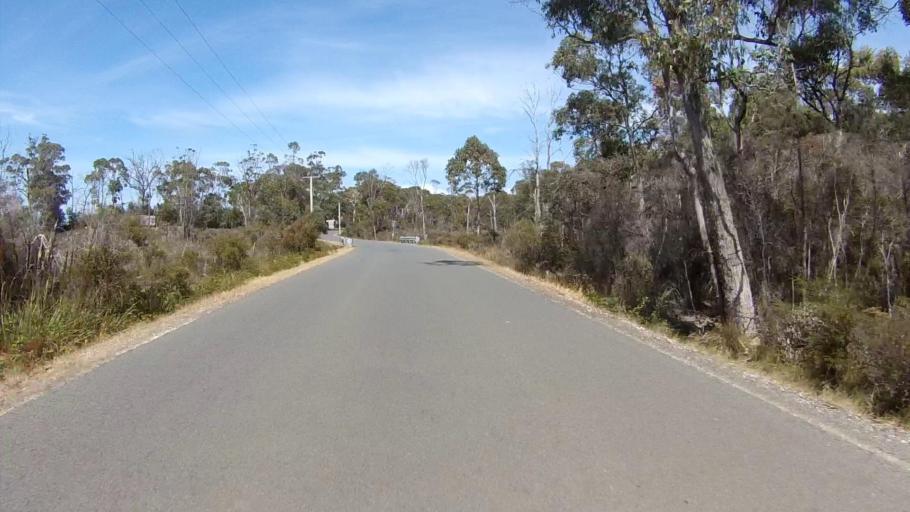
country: AU
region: Tasmania
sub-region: Huon Valley
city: Cygnet
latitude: -43.2414
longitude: 147.1229
